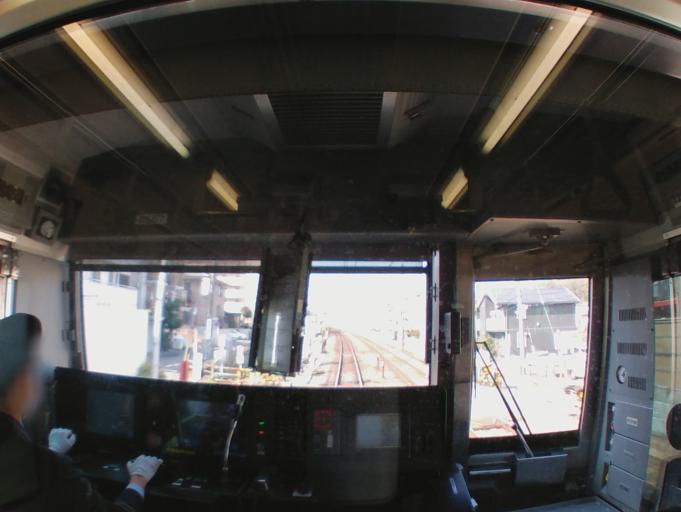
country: JP
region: Tokyo
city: Chofugaoka
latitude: 35.6155
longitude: 139.5522
